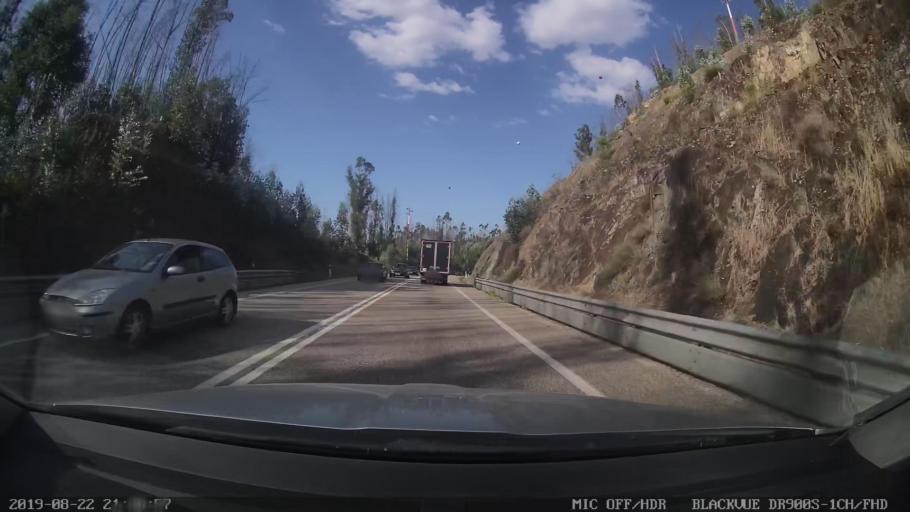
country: PT
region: Leiria
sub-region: Figueiro Dos Vinhos
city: Figueiro dos Vinhos
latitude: 39.9271
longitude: -8.3168
